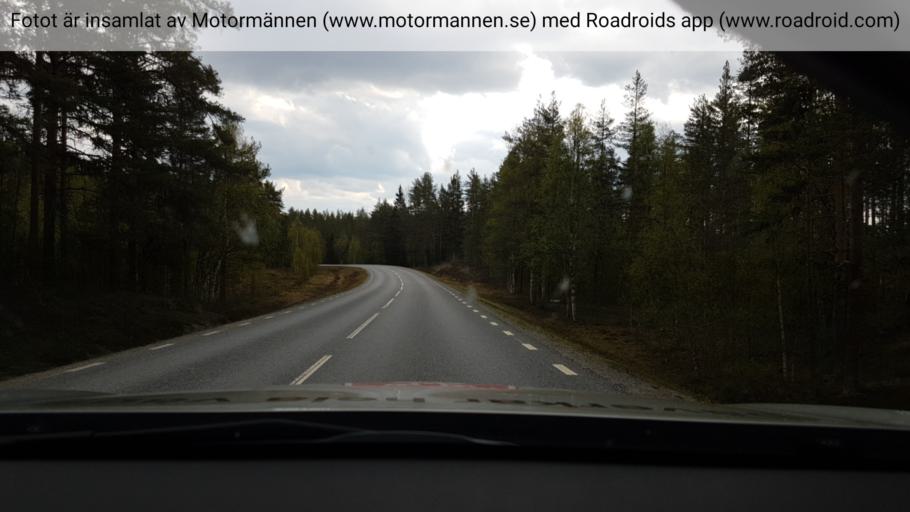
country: SE
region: Vaesterbotten
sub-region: Bjurholms Kommun
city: Bjurholm
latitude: 63.9774
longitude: 18.8141
